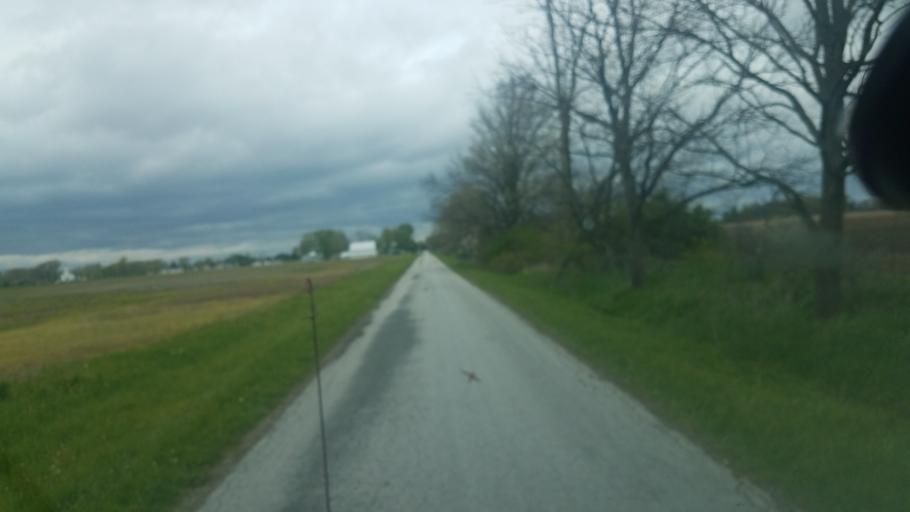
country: US
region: Ohio
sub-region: Marion County
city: Prospect
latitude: 40.5103
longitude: -83.2381
